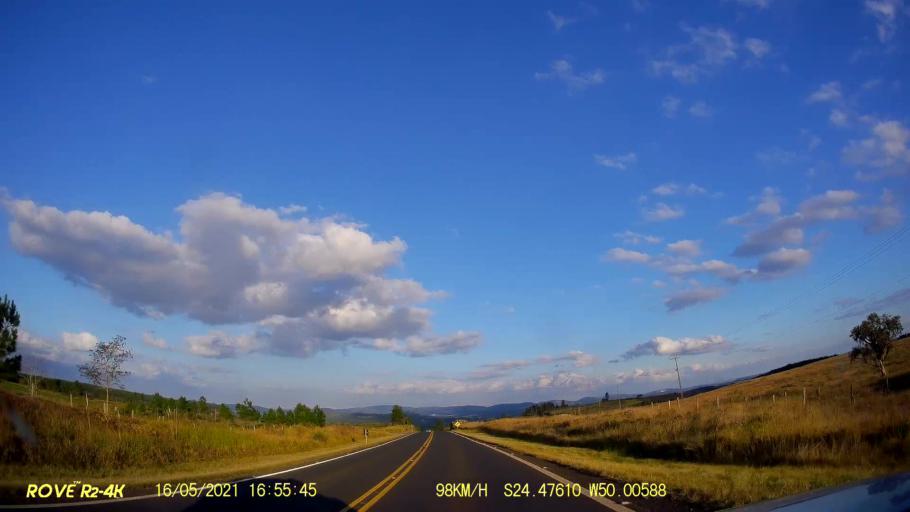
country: BR
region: Parana
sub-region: Pirai Do Sul
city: Pirai do Sul
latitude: -24.4762
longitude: -50.0060
